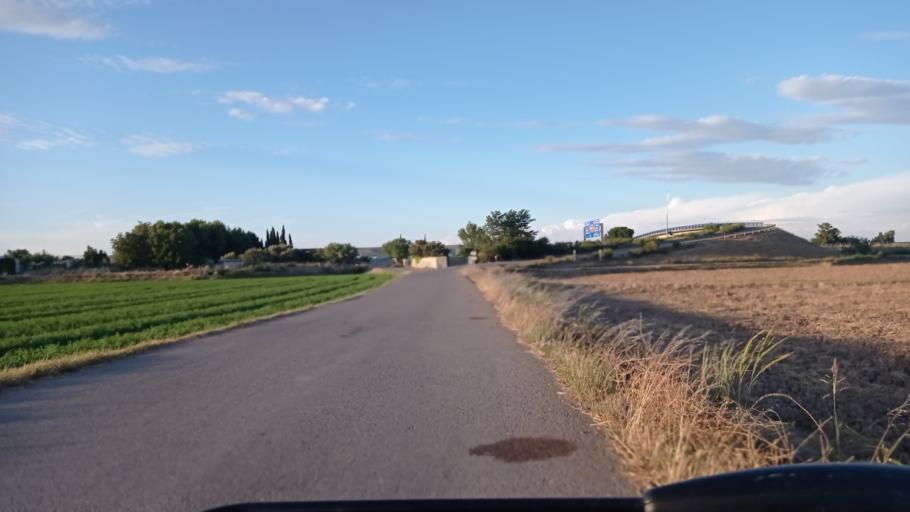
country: ES
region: Aragon
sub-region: Provincia de Zaragoza
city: Oliver-Valdefierro, Oliver, Valdefierro
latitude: 41.6786
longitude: -0.9408
